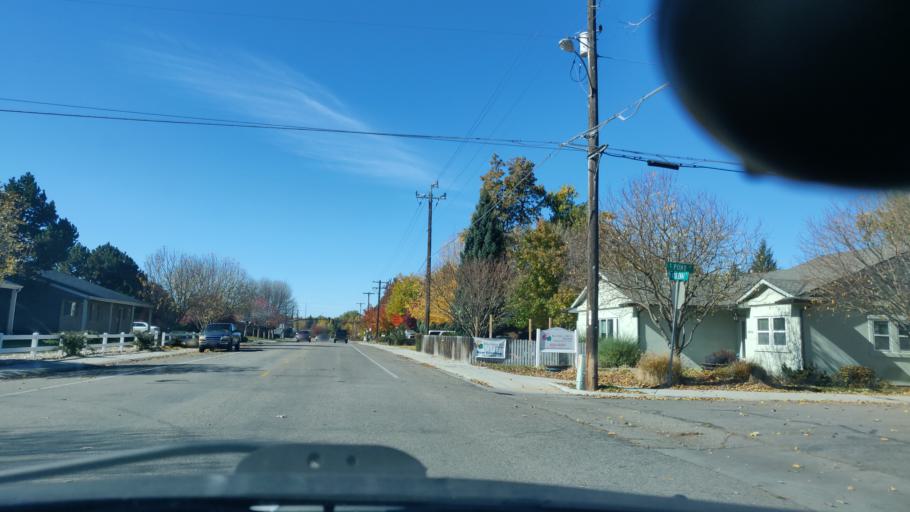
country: US
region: Idaho
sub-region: Ada County
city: Garden City
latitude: 43.5934
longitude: -116.2412
